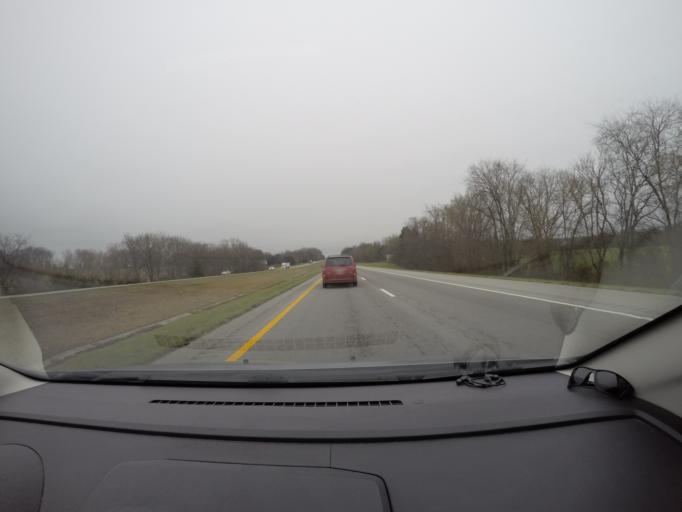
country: US
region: Tennessee
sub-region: Coffee County
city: Manchester
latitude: 35.3719
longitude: -85.9707
